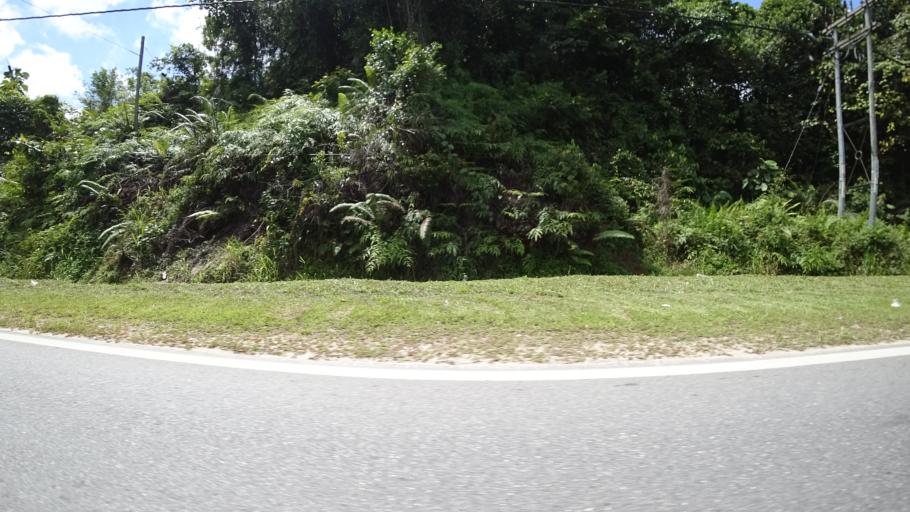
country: MY
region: Sarawak
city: Limbang
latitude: 4.6604
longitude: 114.9492
